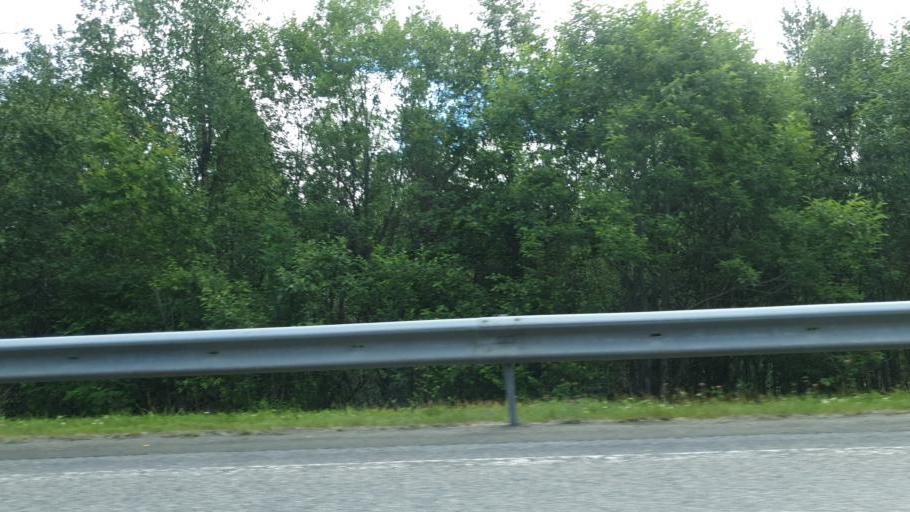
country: NO
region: Sor-Trondelag
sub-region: Rennebu
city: Berkak
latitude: 62.6615
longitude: 9.8913
